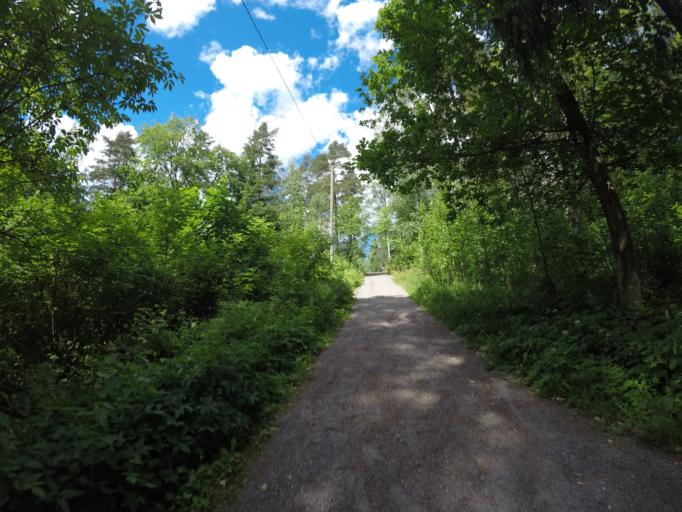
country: FI
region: Haeme
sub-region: Haemeenlinna
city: Haemeenlinna
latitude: 61.0131
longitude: 24.4337
